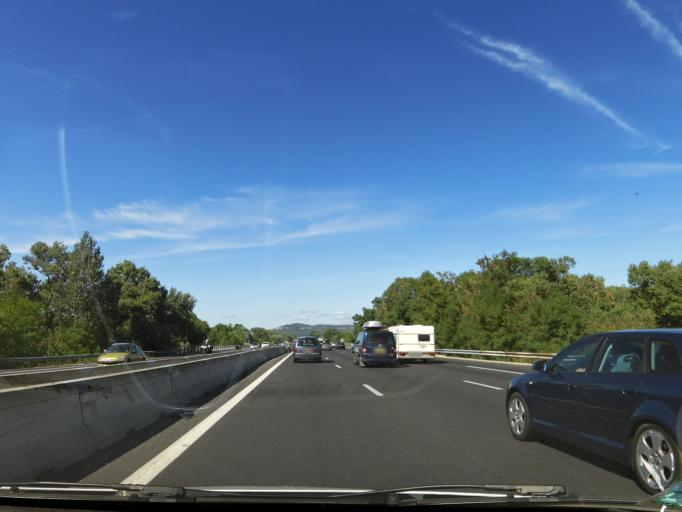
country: FR
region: Provence-Alpes-Cote d'Azur
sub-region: Departement du Vaucluse
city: Mondragon
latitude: 44.2585
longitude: 4.7169
